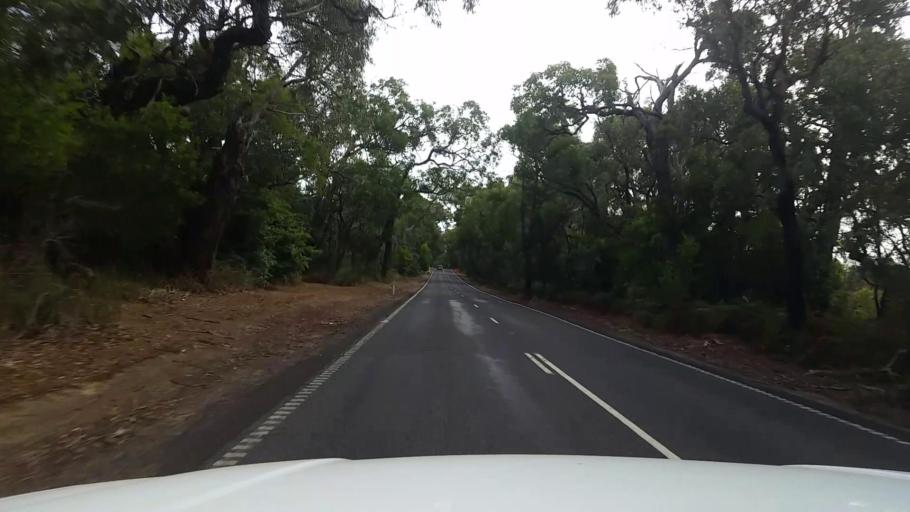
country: AU
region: Victoria
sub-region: Mornington Peninsula
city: Balnarring
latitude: -38.3301
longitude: 145.0940
